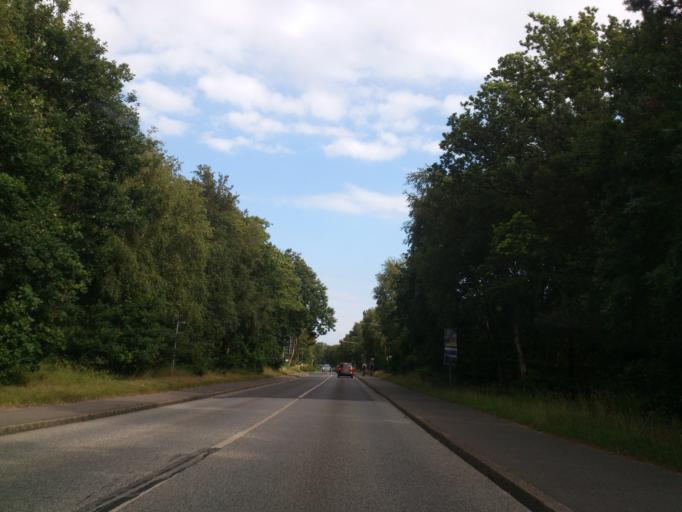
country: DE
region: Schleswig-Holstein
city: Sankt Peter-Ording
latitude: 54.3188
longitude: 8.6116
